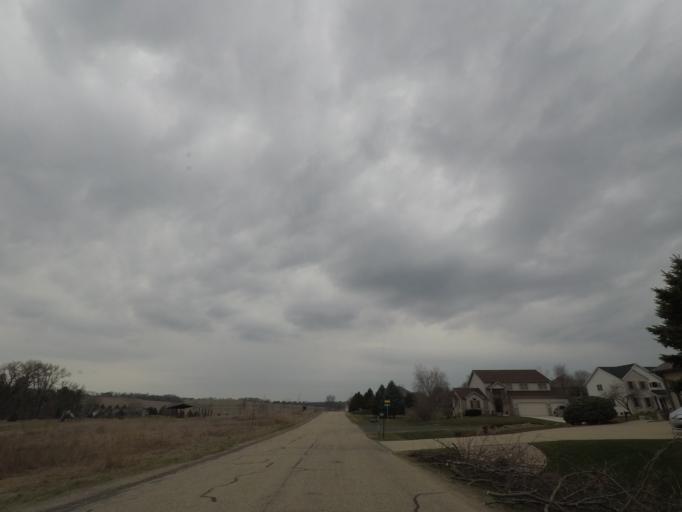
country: US
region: Wisconsin
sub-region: Dane County
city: Middleton
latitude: 43.1135
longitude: -89.5665
